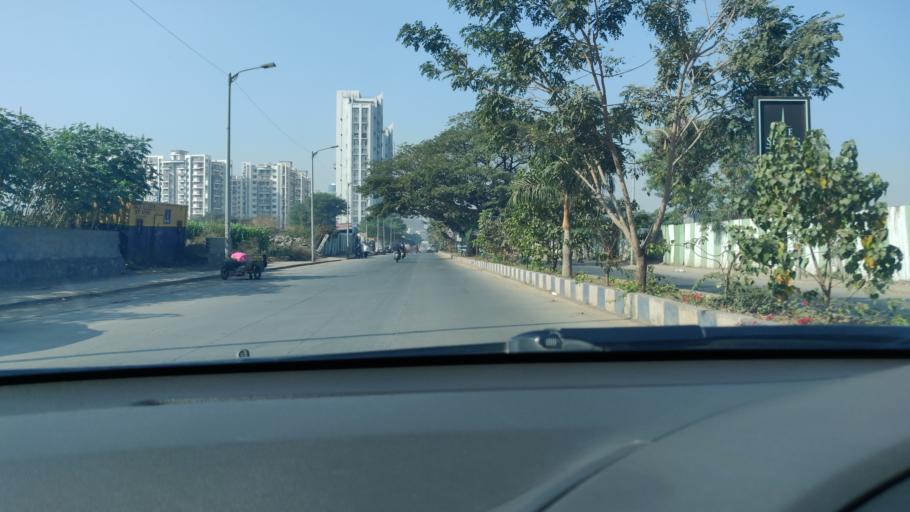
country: IN
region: Maharashtra
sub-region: Pune Division
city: Khadki
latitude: 18.5648
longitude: 73.7990
